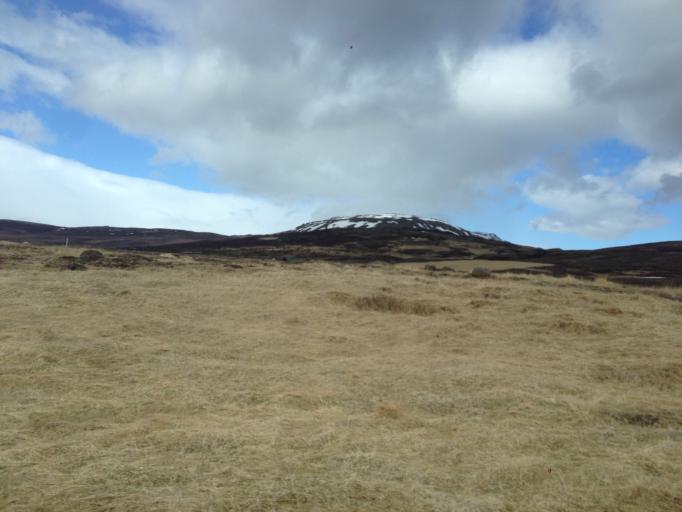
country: IS
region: South
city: Selfoss
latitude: 64.2764
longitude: -20.4137
